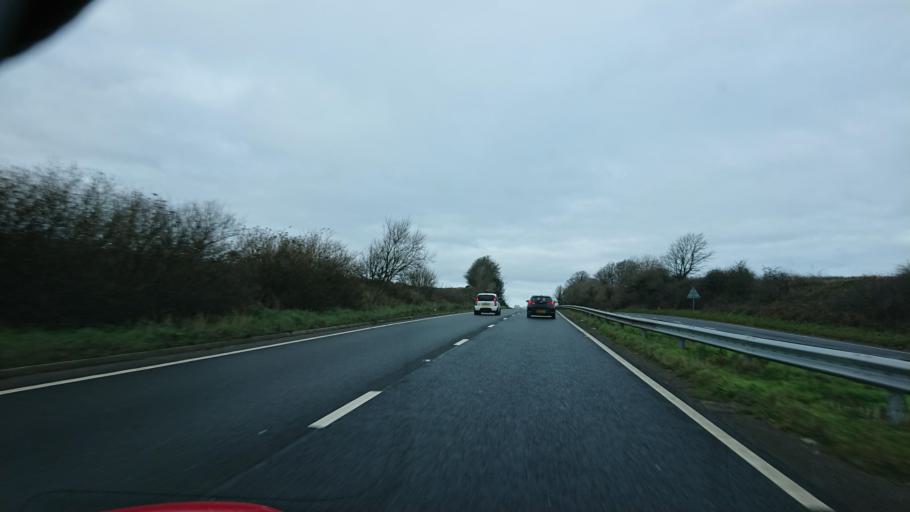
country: GB
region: England
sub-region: Cornwall
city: Liskeard
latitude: 50.4369
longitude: -4.4417
